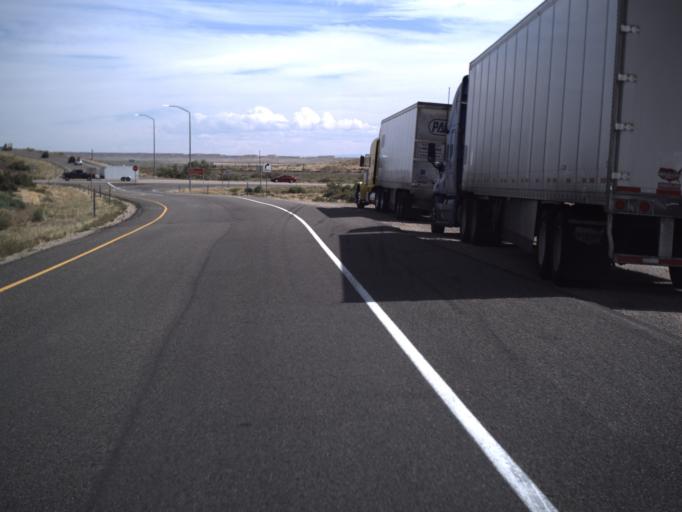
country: US
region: Utah
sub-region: Grand County
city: Moab
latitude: 38.9415
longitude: -109.8192
